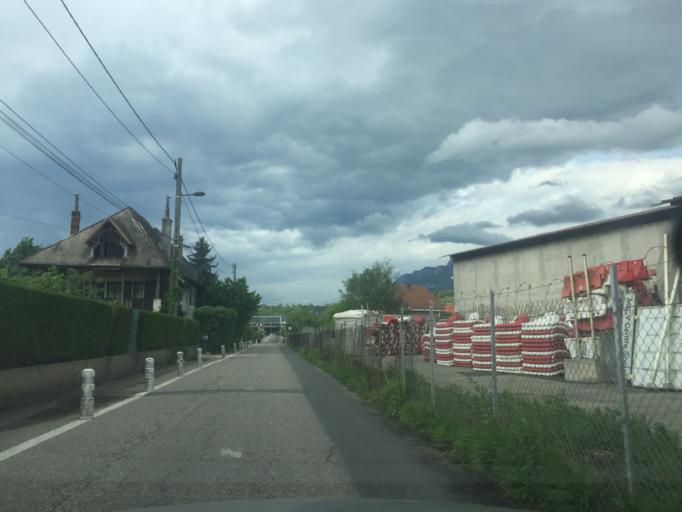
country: FR
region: Rhone-Alpes
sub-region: Departement de la Savoie
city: Cognin
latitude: 45.5813
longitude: 5.9006
